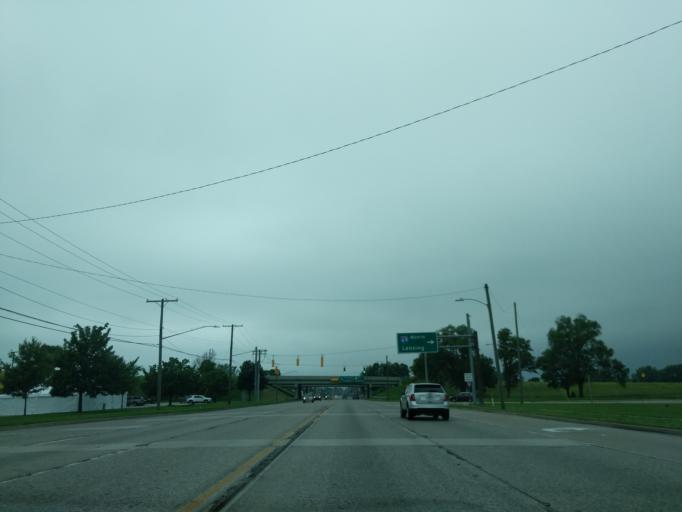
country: US
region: Michigan
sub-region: Branch County
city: Coldwater
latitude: 41.9357
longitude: -84.9704
